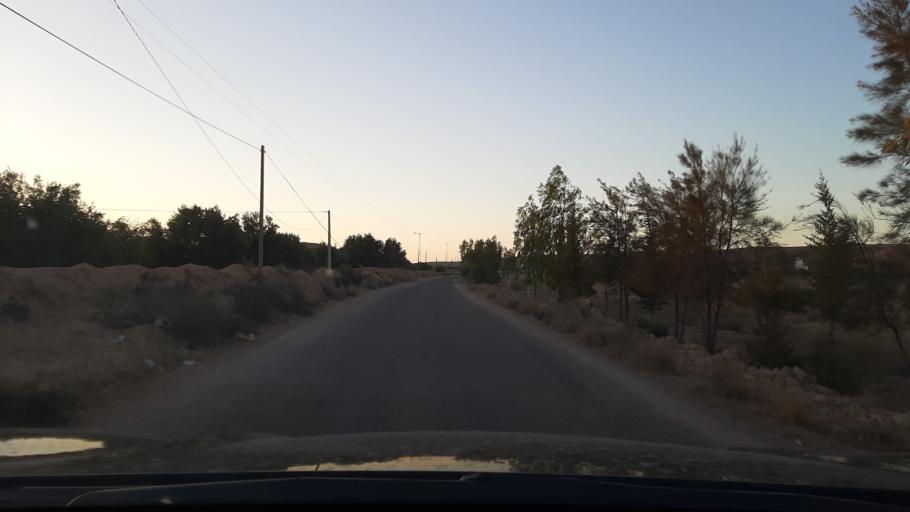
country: TN
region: Qabis
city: Matmata
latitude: 33.5652
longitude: 10.1792
